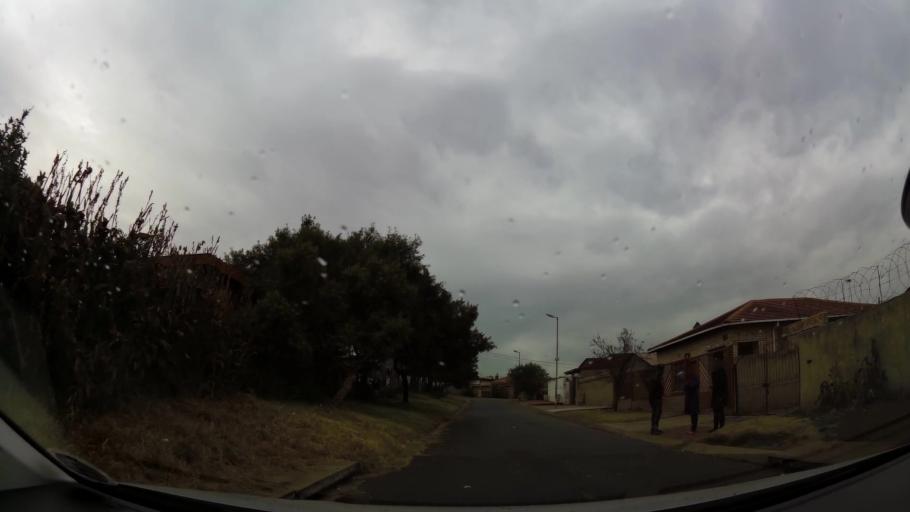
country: ZA
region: Gauteng
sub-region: City of Johannesburg Metropolitan Municipality
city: Soweto
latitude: -26.2439
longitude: 27.8762
